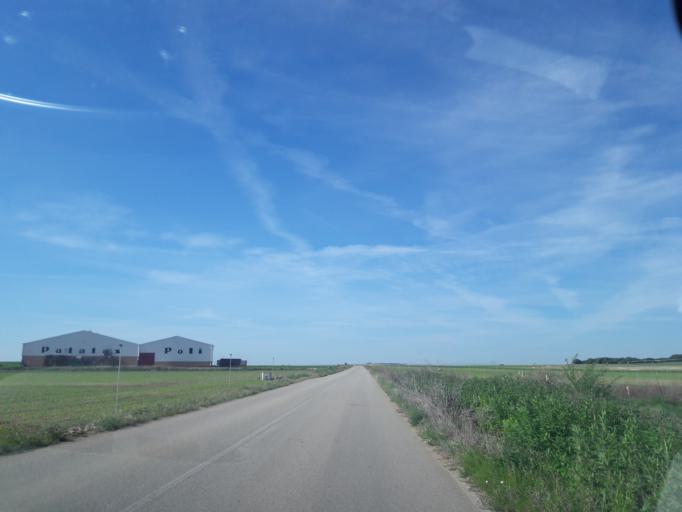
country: ES
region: Castille and Leon
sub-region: Provincia de Salamanca
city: Villoruela
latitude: 41.0367
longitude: -5.3884
